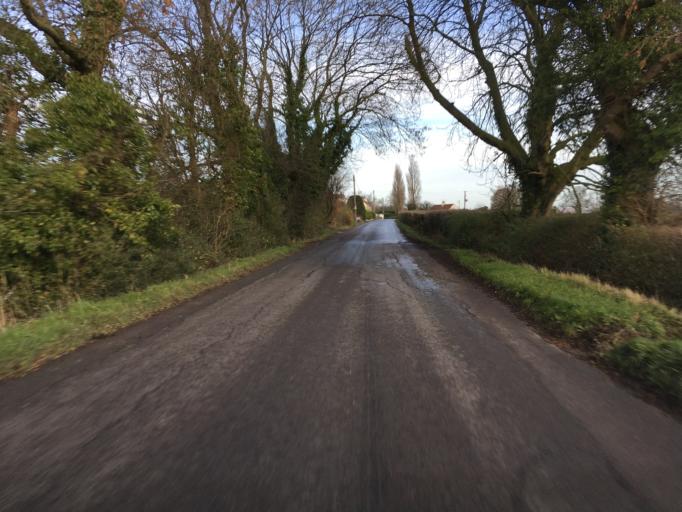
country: GB
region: England
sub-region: South Gloucestershire
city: Tytherington
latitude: 51.5682
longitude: -2.5025
